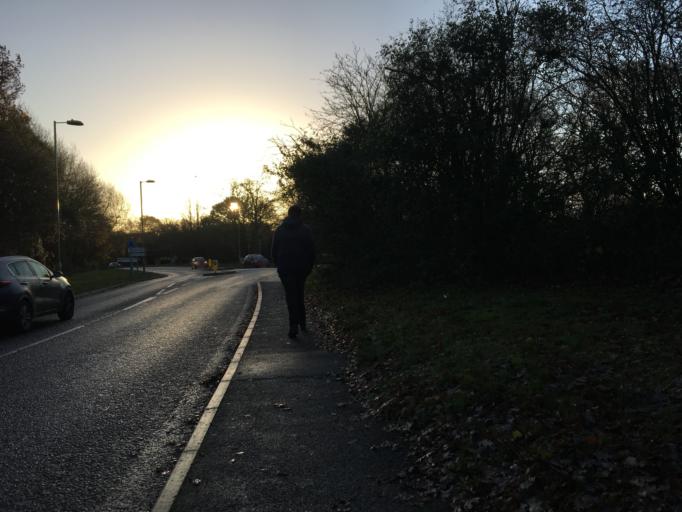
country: GB
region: England
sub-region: Hampshire
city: Old Basing
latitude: 51.2826
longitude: -1.0610
